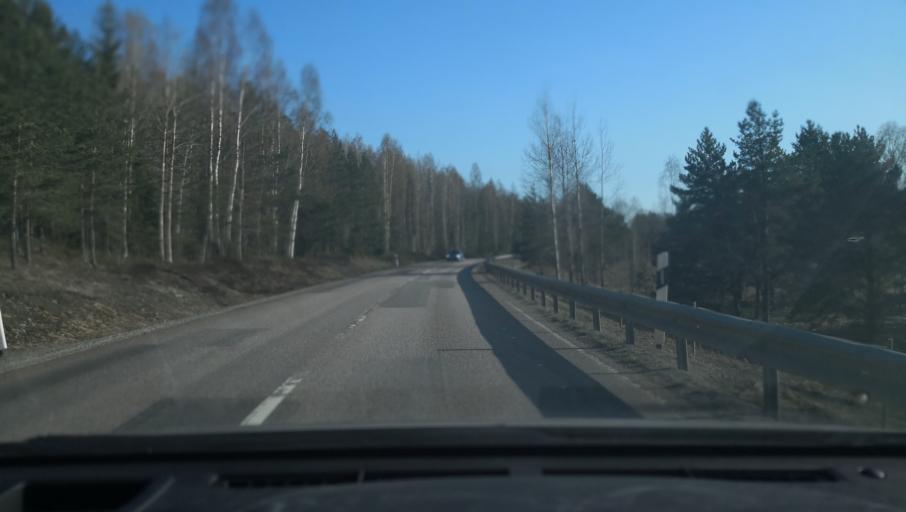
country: SE
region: Uppsala
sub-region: Heby Kommun
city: Heby
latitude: 59.9971
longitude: 16.8324
